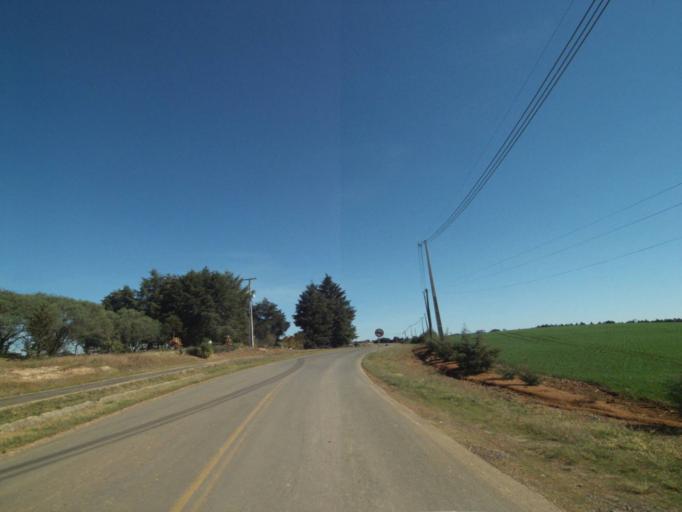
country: BR
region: Parana
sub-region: Tibagi
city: Tibagi
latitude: -24.5226
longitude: -50.4302
